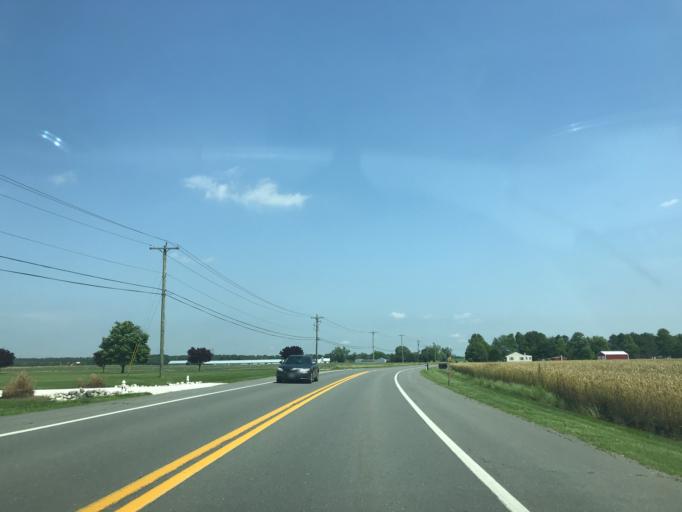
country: US
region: Maryland
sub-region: Dorchester County
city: Hurlock
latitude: 38.5970
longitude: -75.9008
